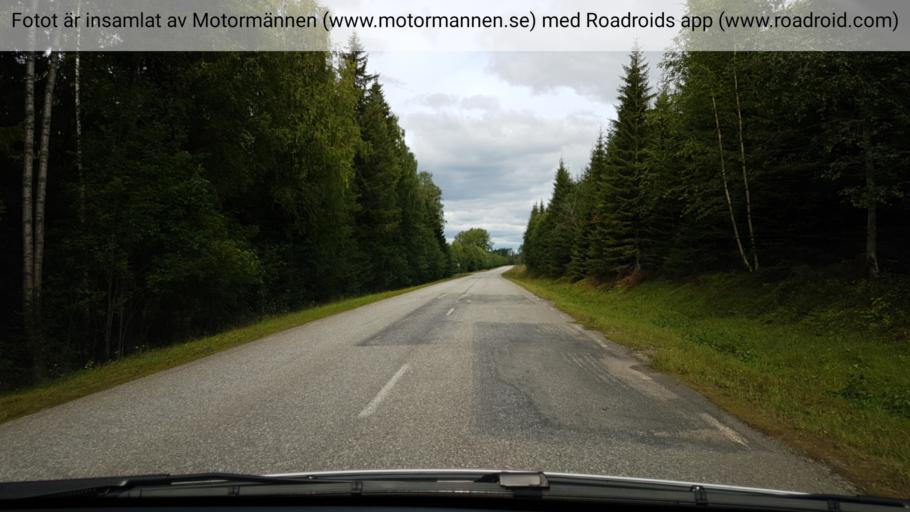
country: SE
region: Vaesterbotten
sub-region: Vannas Kommun
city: Vannasby
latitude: 64.0590
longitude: 19.9347
